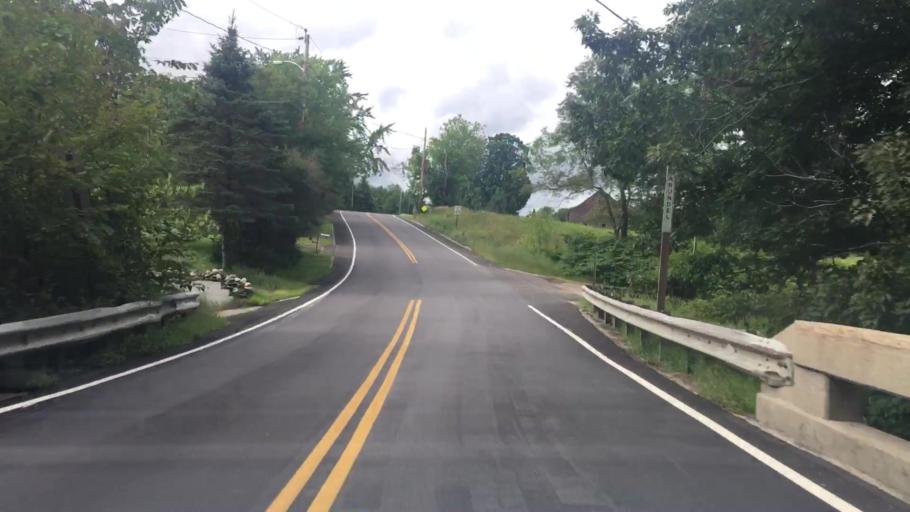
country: US
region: Maine
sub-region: York County
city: West Kennebunk
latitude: 43.4576
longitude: -70.6056
